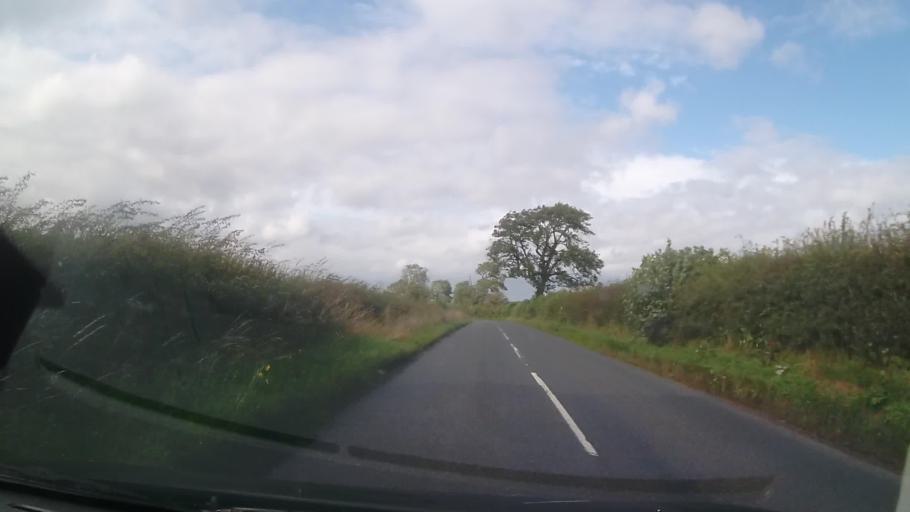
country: GB
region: Wales
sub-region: Sir Powys
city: Knighton
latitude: 52.4010
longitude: -3.0451
